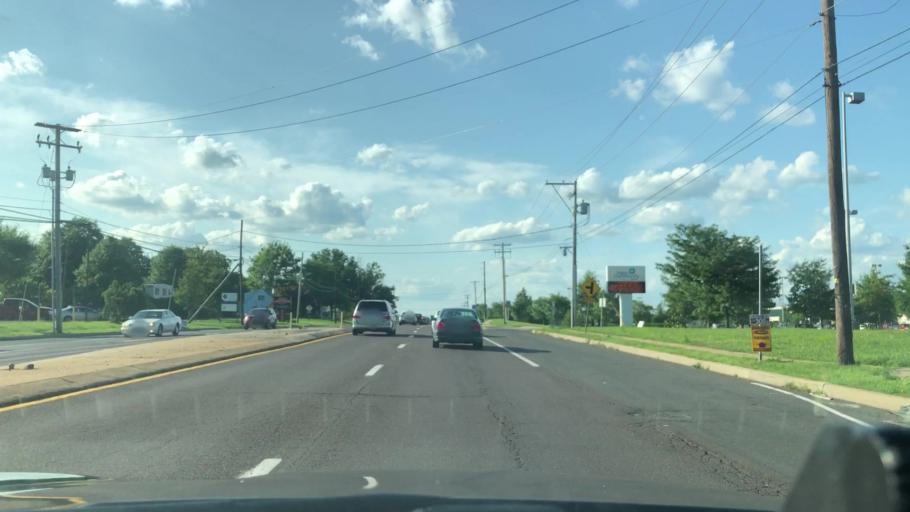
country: US
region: Pennsylvania
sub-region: Bucks County
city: Quakertown
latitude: 40.4179
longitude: -75.3442
